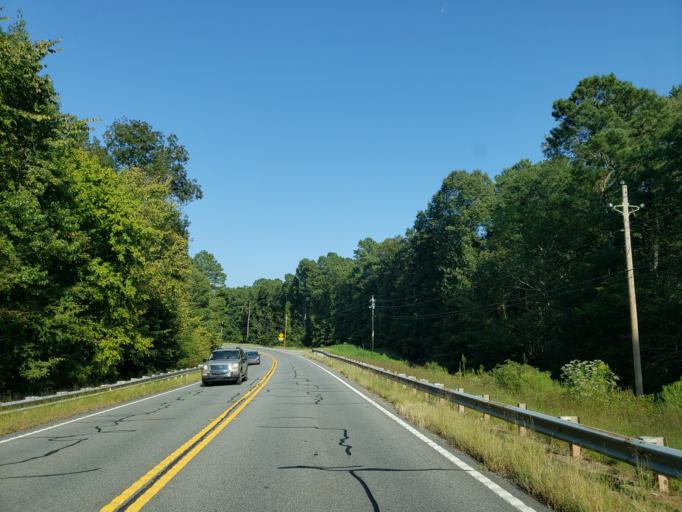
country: US
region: Georgia
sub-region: Whitfield County
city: Varnell
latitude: 34.8952
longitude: -84.9310
